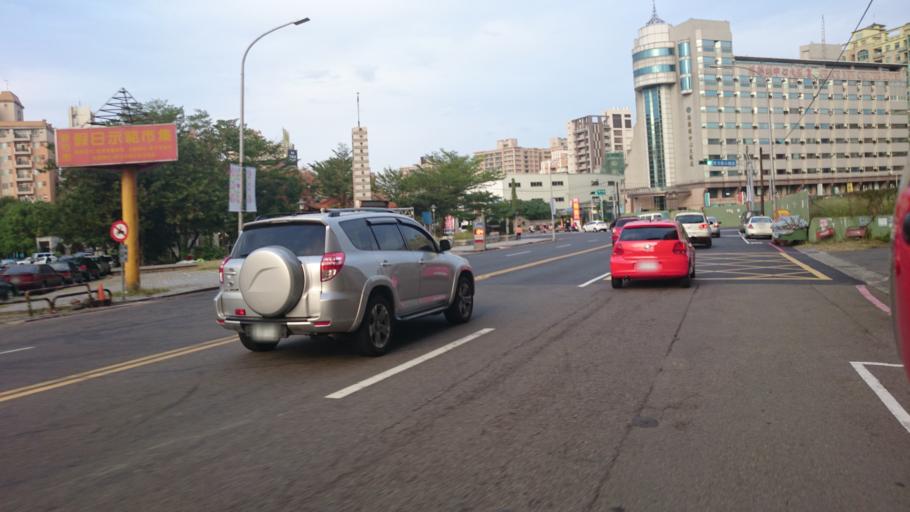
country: TW
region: Taiwan
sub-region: Hsinchu
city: Hsinchu
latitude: 24.8004
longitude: 120.9819
